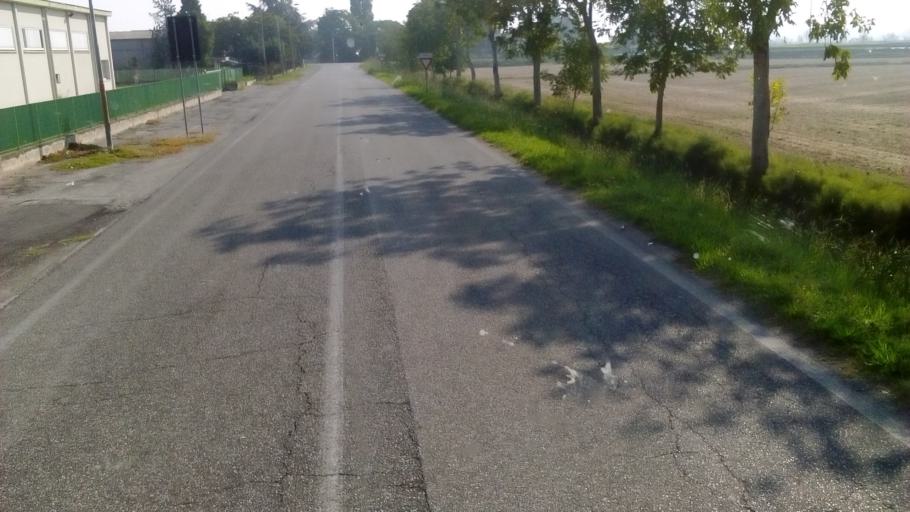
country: IT
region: Lombardy
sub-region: Provincia di Mantova
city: Ostiglia
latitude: 45.0870
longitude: 11.1361
